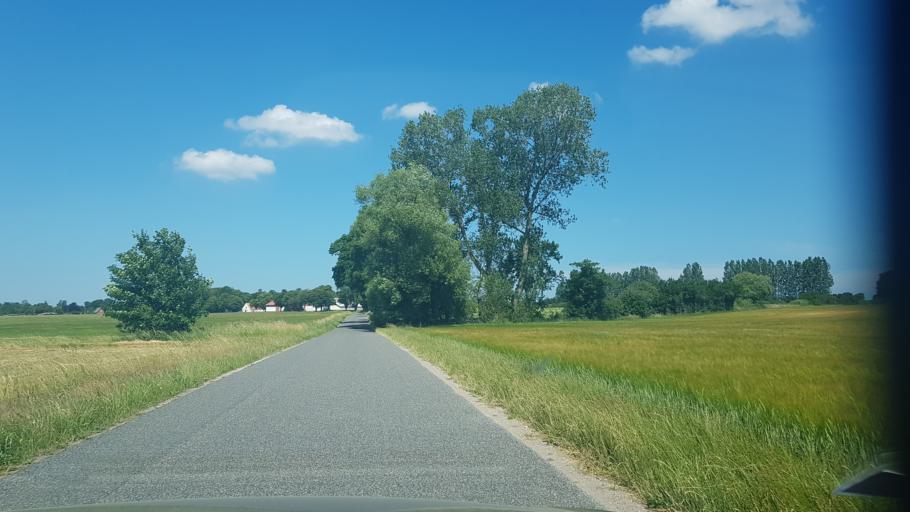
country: DK
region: Zealand
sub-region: Kalundborg Kommune
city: Svebolle
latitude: 55.7024
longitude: 11.2880
